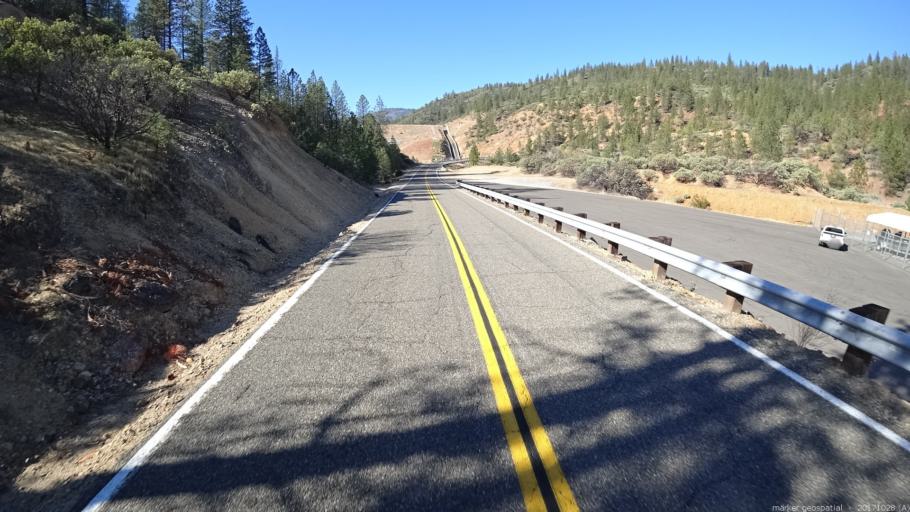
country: US
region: California
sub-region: Shasta County
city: Shasta
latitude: 40.6281
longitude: -122.4683
